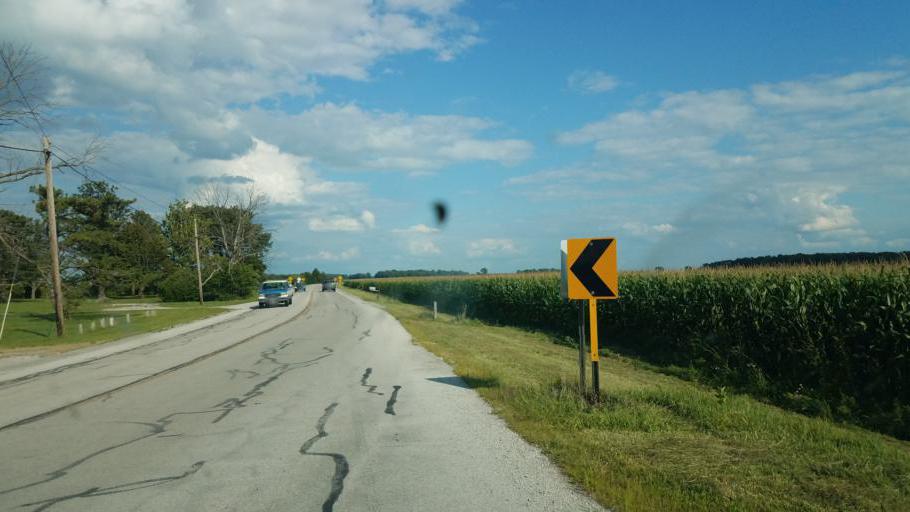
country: US
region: Ohio
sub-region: Wood County
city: Bowling Green
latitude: 41.3629
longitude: -83.5711
